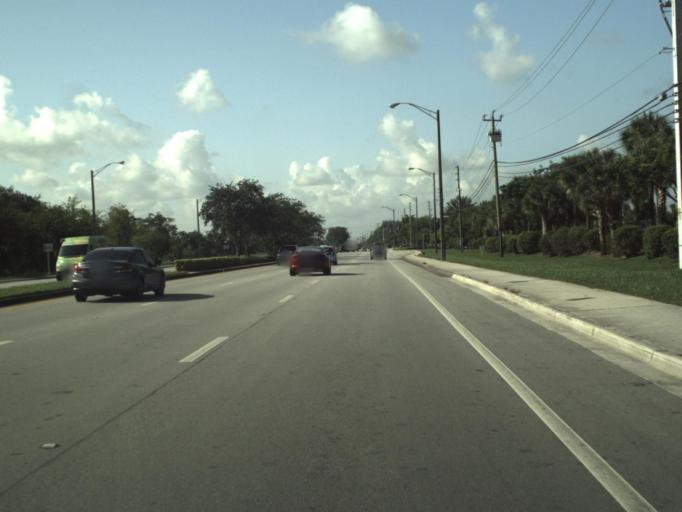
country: US
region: Florida
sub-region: Broward County
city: Parkland
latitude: 26.3228
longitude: -80.2029
